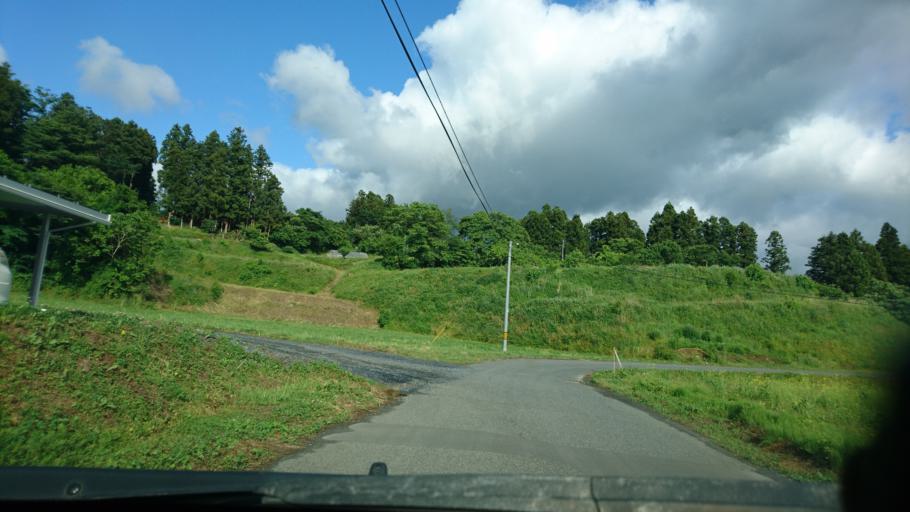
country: JP
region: Iwate
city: Ichinoseki
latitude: 38.8560
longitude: 141.2868
